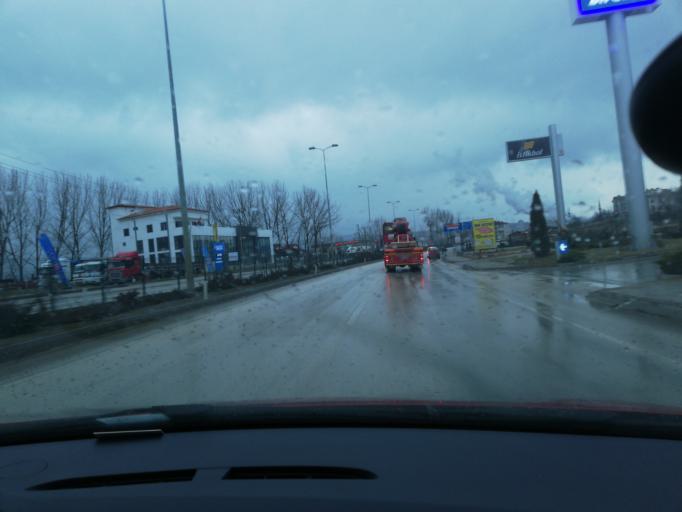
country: TR
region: Kastamonu
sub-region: Cide
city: Kastamonu
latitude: 41.4231
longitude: 33.8021
